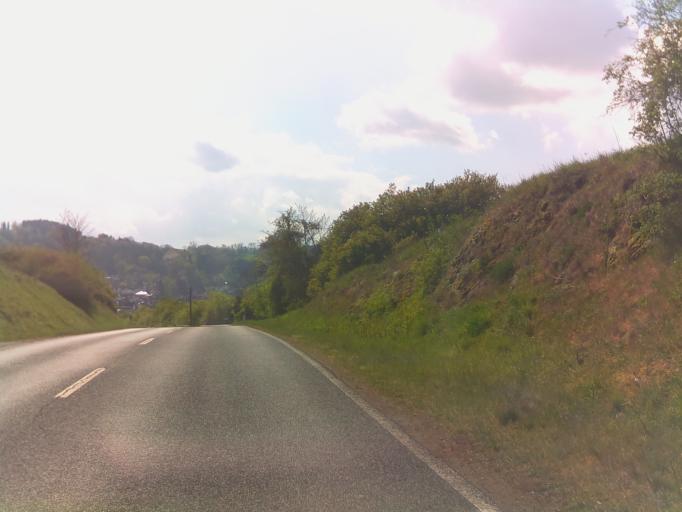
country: DE
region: Hesse
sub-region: Regierungsbezirk Giessen
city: Wetzlar
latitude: 50.5706
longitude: 8.5366
